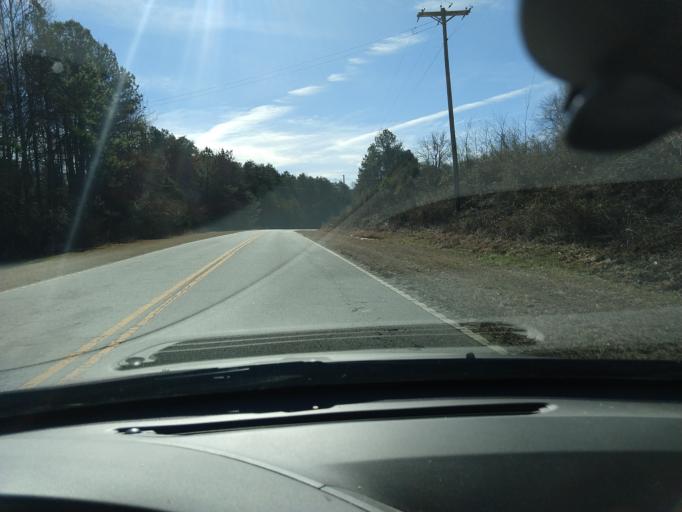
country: US
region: South Carolina
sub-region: Oconee County
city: Westminster
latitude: 34.6233
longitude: -83.1368
